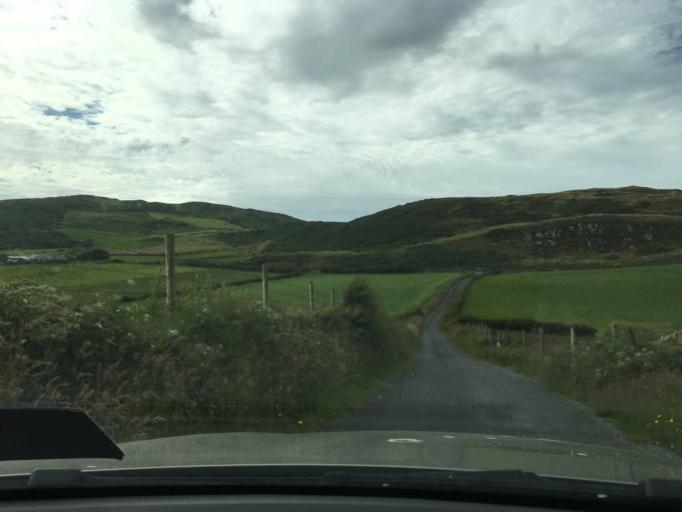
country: IE
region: Ulster
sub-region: County Donegal
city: Carndonagh
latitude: 55.3286
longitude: -7.3183
